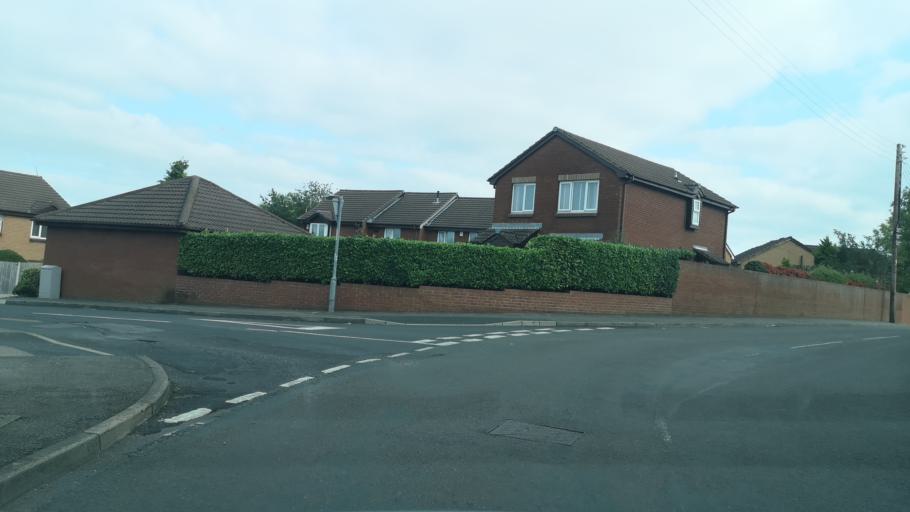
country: GB
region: England
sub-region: City and Borough of Wakefield
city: Crigglestone
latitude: 53.6381
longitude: -1.5304
